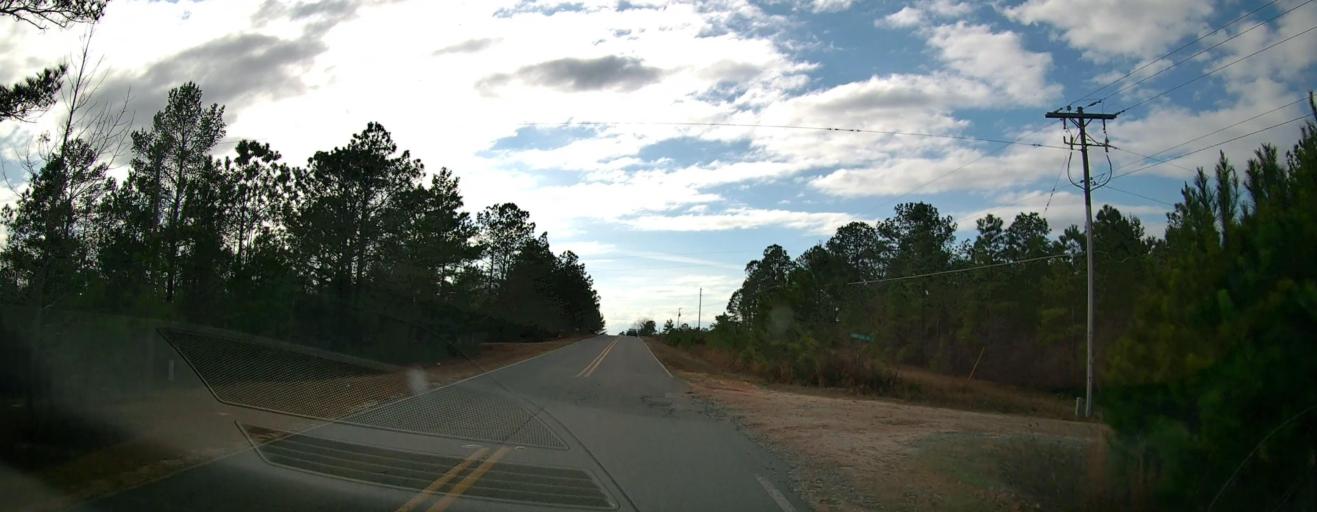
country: US
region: Georgia
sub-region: Talbot County
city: Talbotton
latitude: 32.4988
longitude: -84.5693
